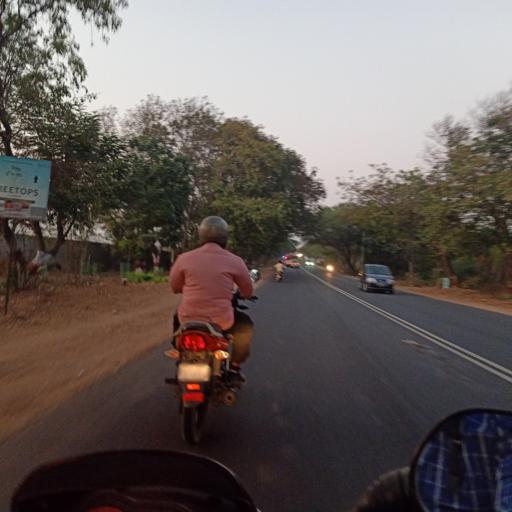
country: IN
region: Telangana
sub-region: Rangareddi
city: Secunderabad
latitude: 17.5491
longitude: 78.5356
